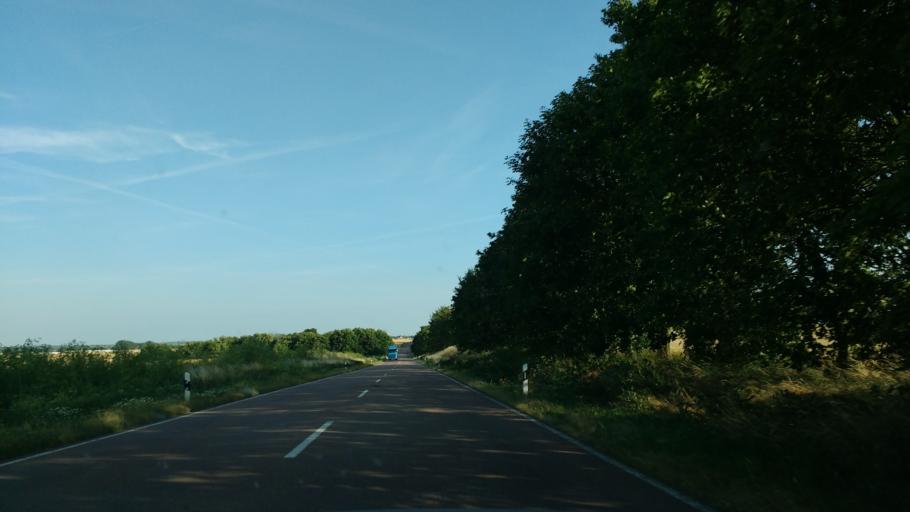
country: DE
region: Saxony-Anhalt
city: Querfurt
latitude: 51.4004
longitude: 11.5884
